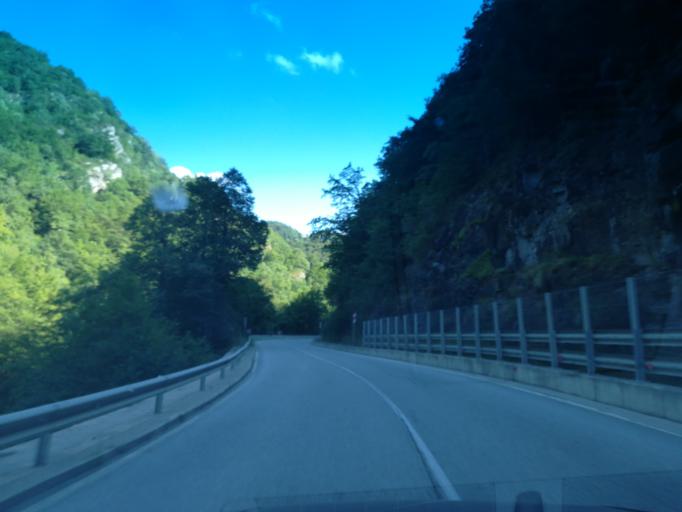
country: BG
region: Smolyan
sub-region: Obshtina Chepelare
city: Chepelare
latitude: 41.7883
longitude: 24.7095
